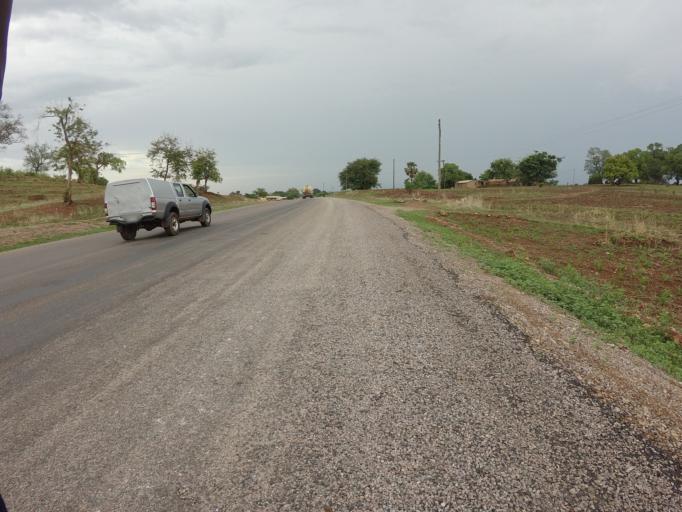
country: GH
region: Upper East
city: Bolgatanga
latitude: 10.8433
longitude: -0.6900
